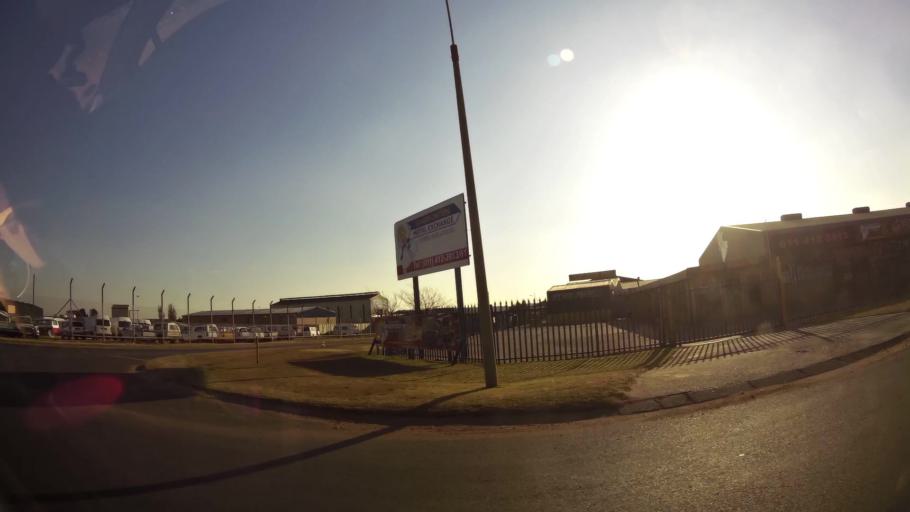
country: ZA
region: Gauteng
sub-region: West Rand District Municipality
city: Randfontein
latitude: -26.1998
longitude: 27.6964
